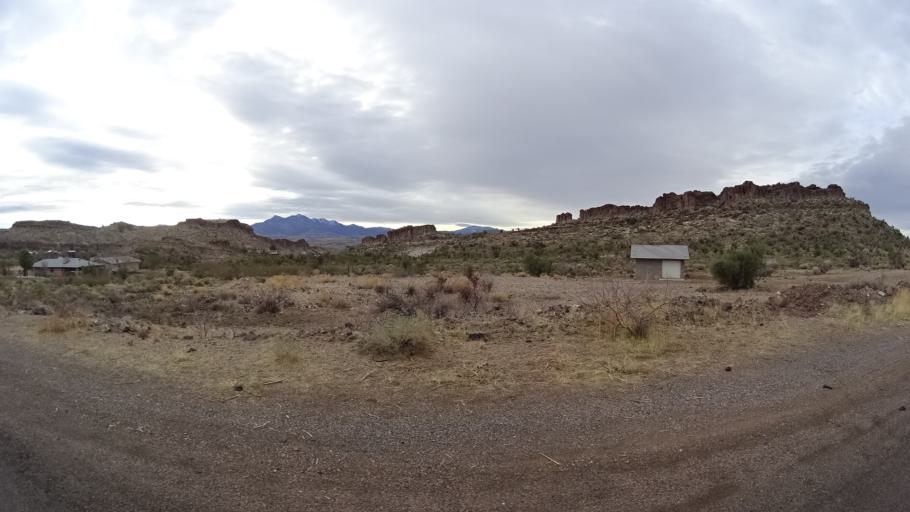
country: US
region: Arizona
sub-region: Mohave County
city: Kingman
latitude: 35.2156
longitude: -114.0756
